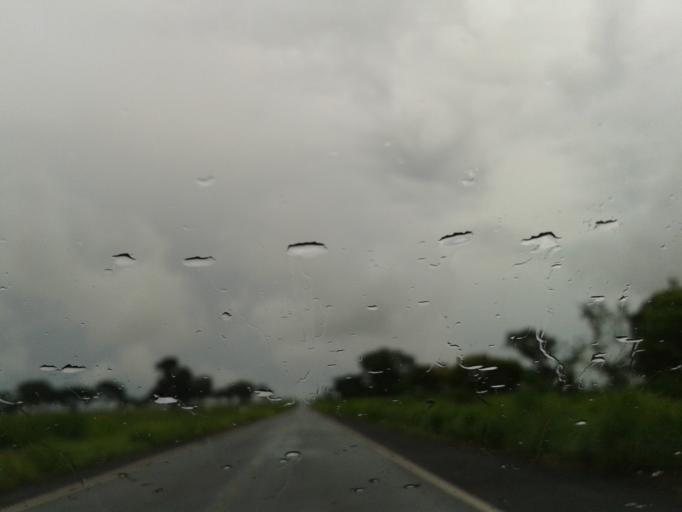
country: BR
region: Minas Gerais
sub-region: Santa Vitoria
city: Santa Vitoria
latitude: -19.1577
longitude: -50.1192
